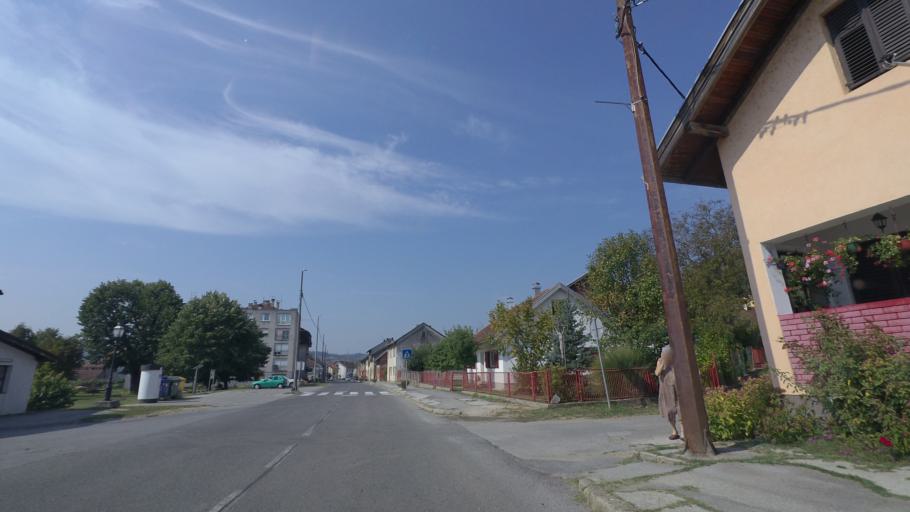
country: BA
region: Republika Srpska
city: Kostajnica
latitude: 45.2246
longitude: 16.5554
